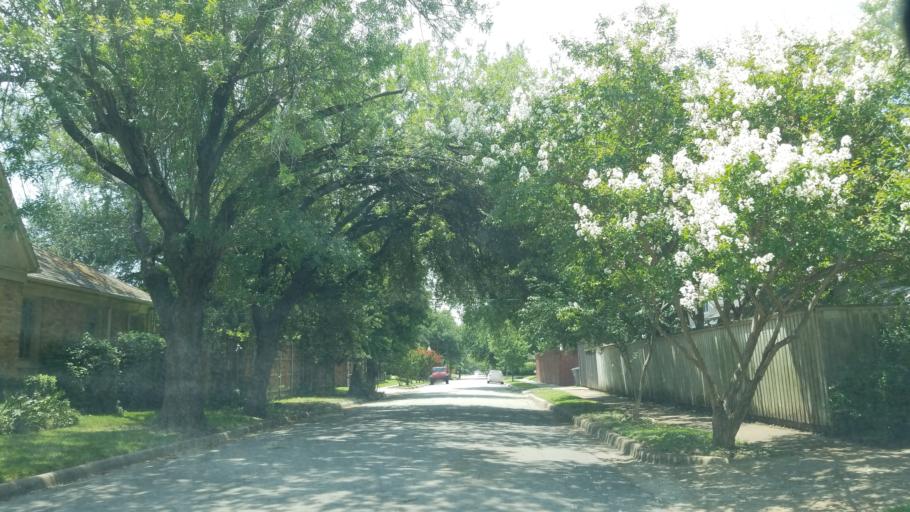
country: US
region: Texas
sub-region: Dallas County
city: Highland Park
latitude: 32.8254
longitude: -96.7723
